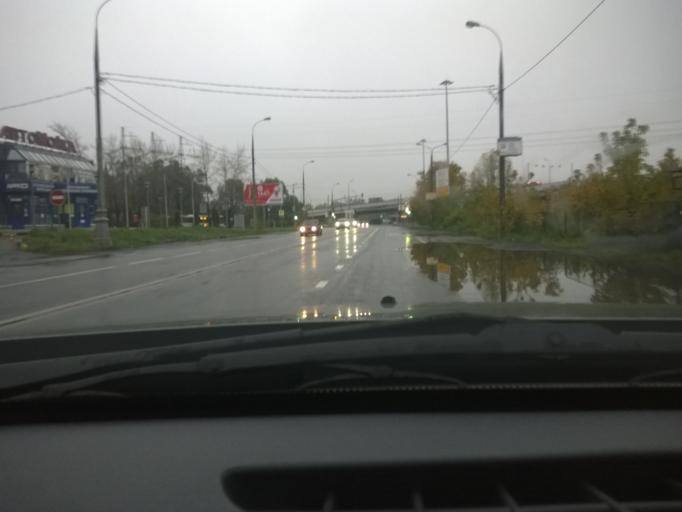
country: RU
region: Moscow
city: Zhulebino
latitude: 55.7103
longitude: 37.8511
